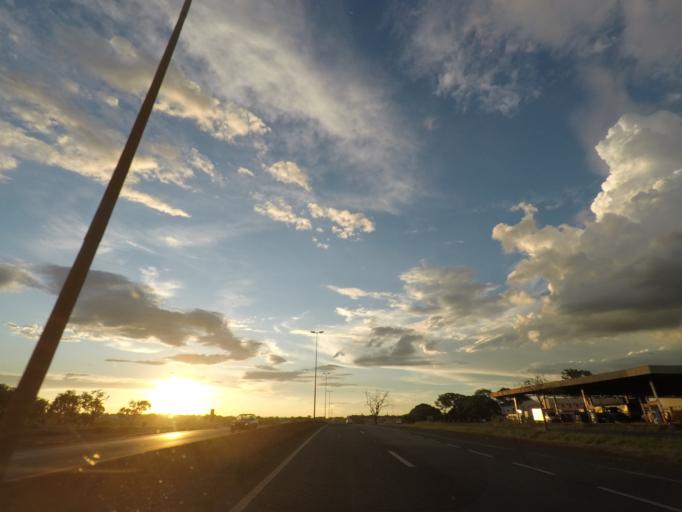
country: BR
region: Minas Gerais
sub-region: Uberaba
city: Uberaba
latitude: -19.7792
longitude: -47.9574
